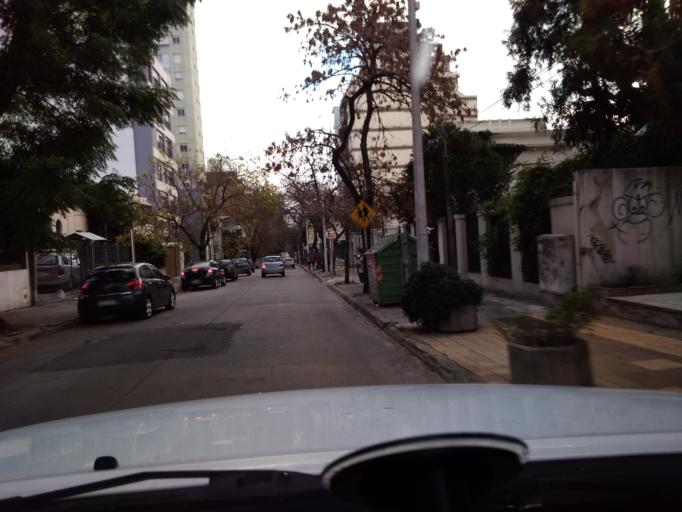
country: UY
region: Montevideo
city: Montevideo
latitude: -34.9094
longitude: -56.1560
